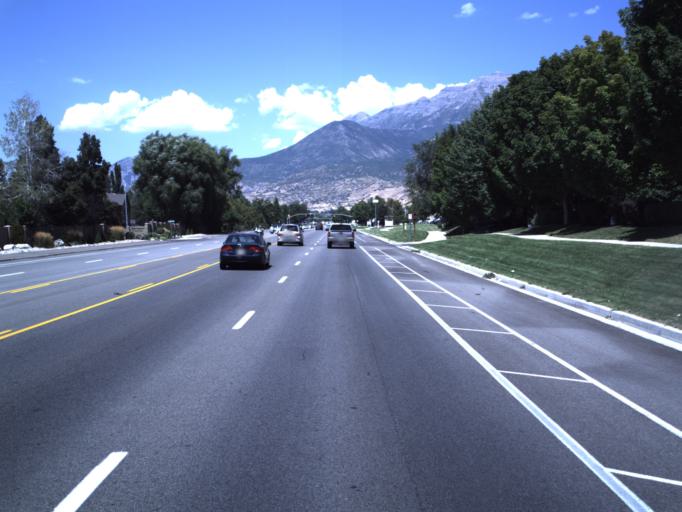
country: US
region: Utah
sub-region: Utah County
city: Provo
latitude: 40.2737
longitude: -111.6572
